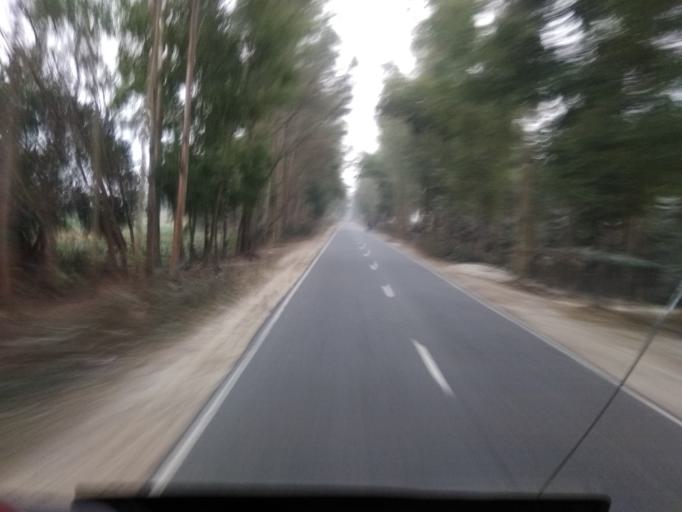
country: BD
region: Rajshahi
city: Bogra
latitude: 24.6671
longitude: 89.2740
